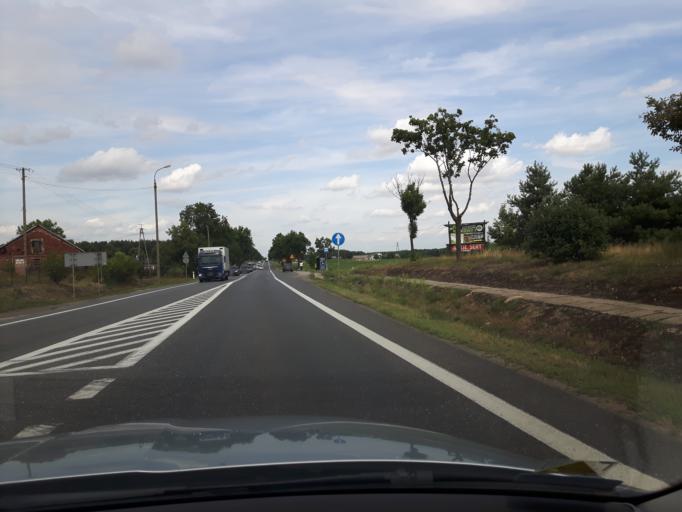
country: PL
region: Masovian Voivodeship
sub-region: Powiat mlawski
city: Strzegowo
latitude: 52.9632
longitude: 20.3027
